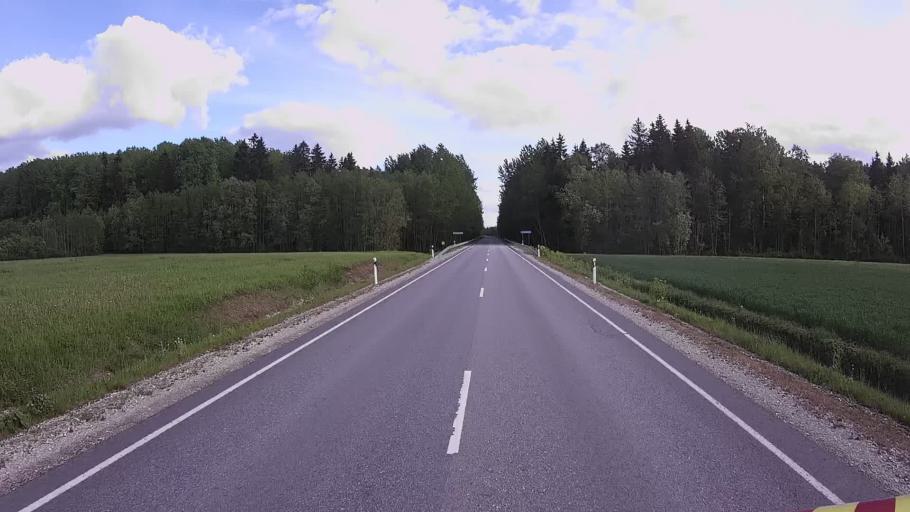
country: EE
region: Jogevamaa
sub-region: Mustvee linn
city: Mustvee
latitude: 58.8864
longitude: 26.8131
